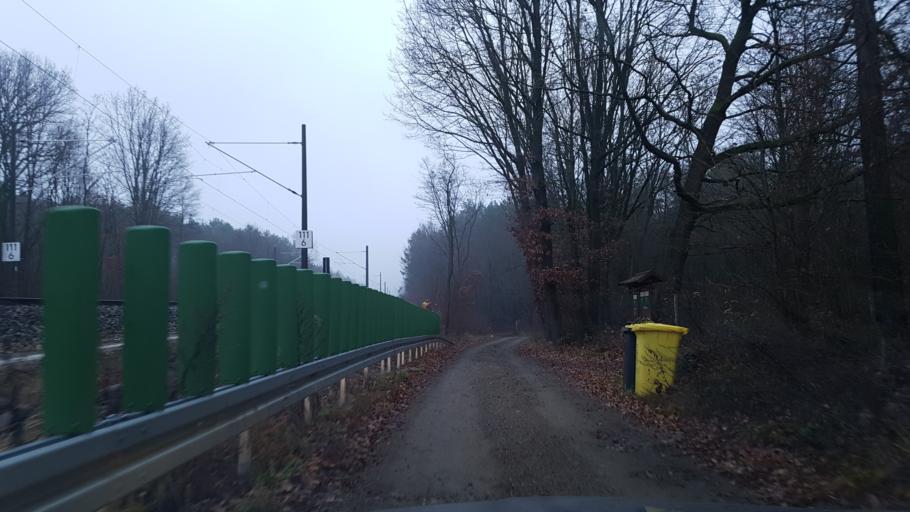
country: DE
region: Brandenburg
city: Ruckersdorf
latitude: 51.5435
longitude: 13.5760
